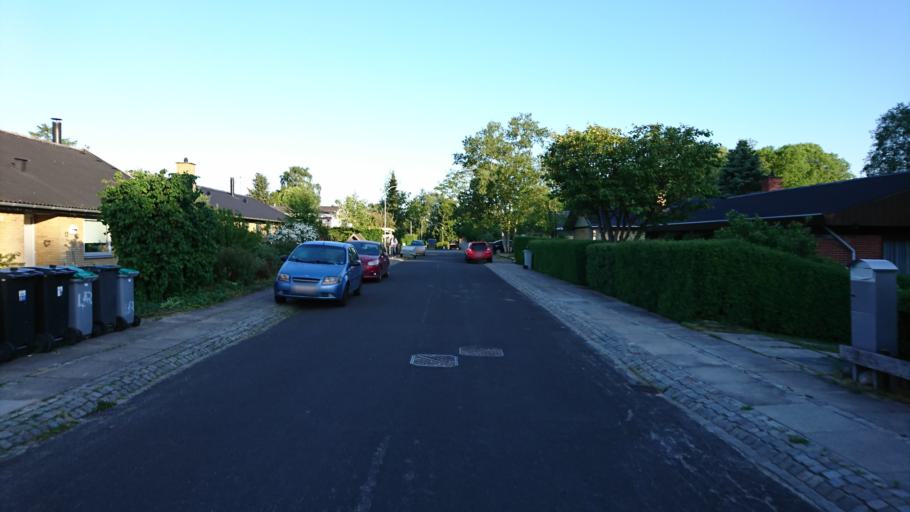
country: DK
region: Capital Region
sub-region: Ballerup Kommune
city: Malov
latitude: 55.7514
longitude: 12.3473
